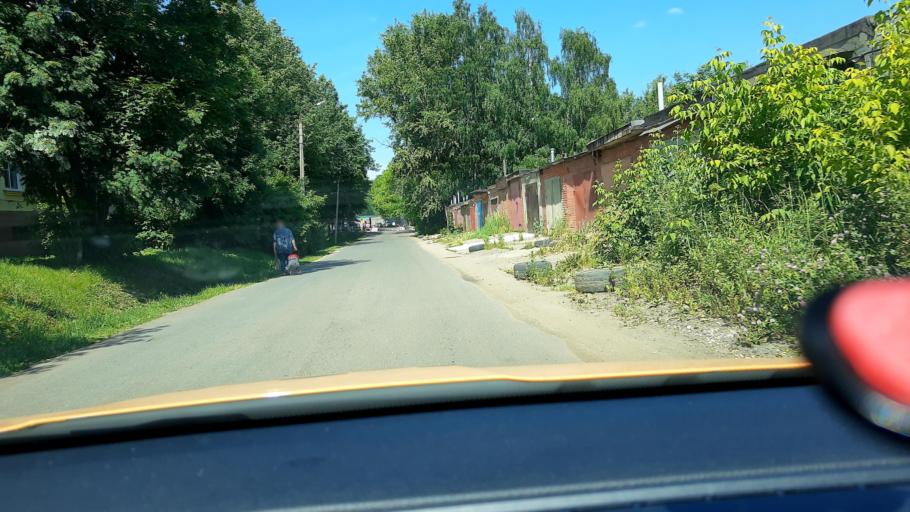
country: RU
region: Moskovskaya
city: Dolgoprudnyy
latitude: 55.9502
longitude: 37.5269
